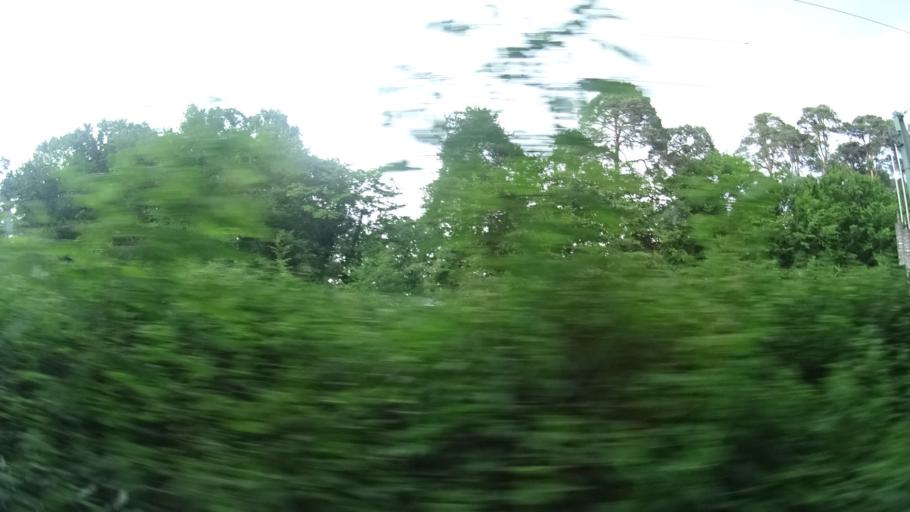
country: DE
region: Rheinland-Pfalz
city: Schifferstadt
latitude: 49.3694
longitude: 8.3819
